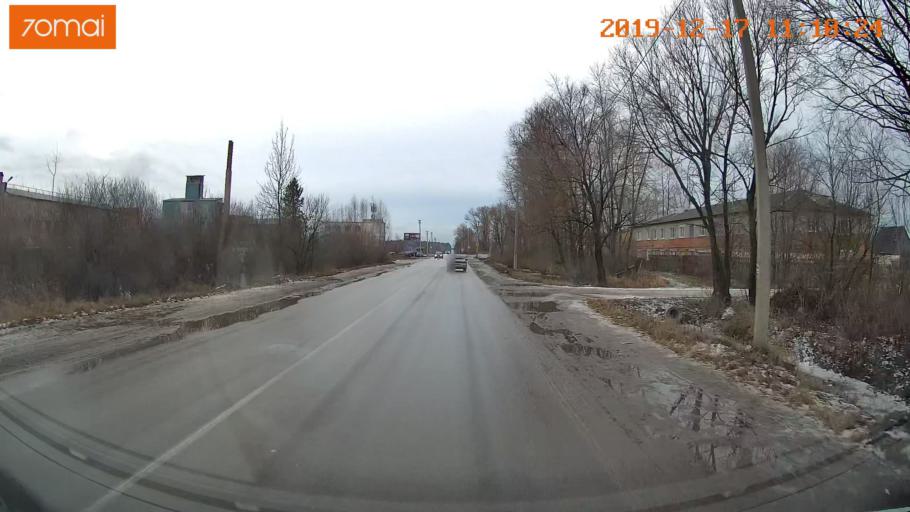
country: RU
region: Vladimir
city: Gus'-Khrustal'nyy
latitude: 55.5930
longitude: 40.6417
